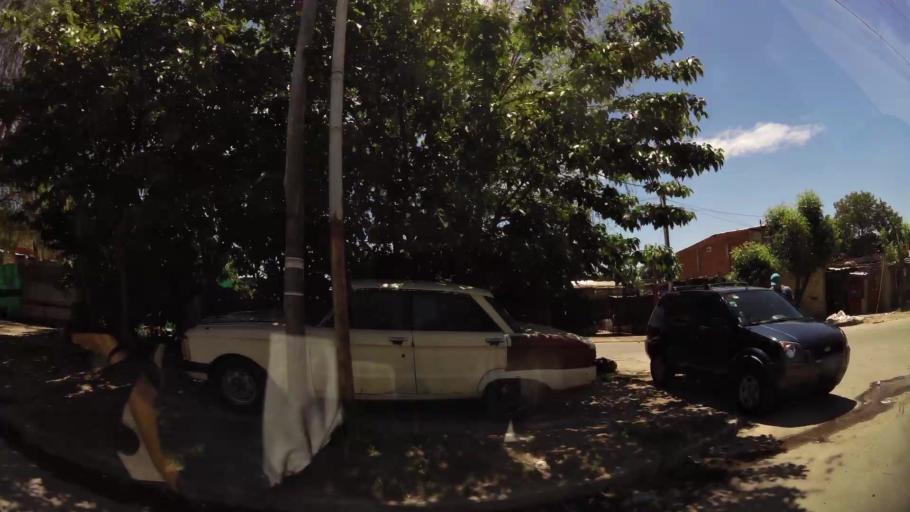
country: AR
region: Buenos Aires
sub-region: Partido de Lanus
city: Lanus
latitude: -34.7259
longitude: -58.3322
